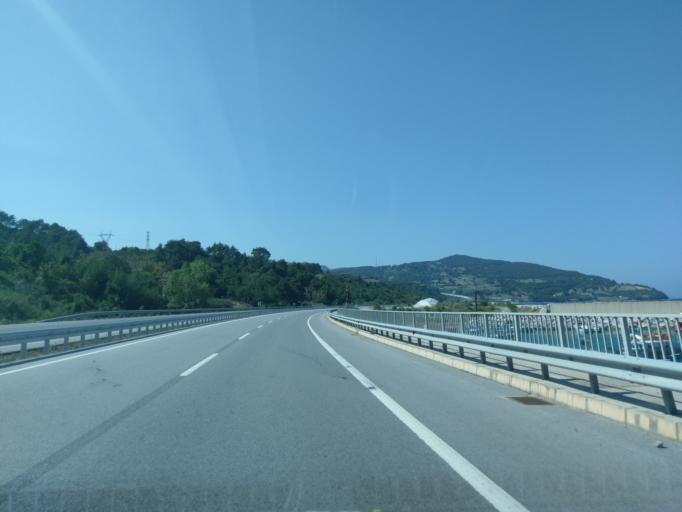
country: TR
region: Sinop
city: Dikmen
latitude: 41.7153
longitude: 35.2777
